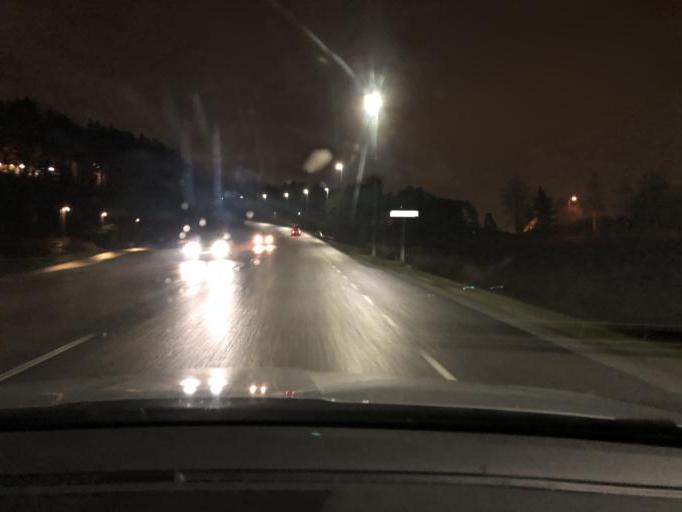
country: SE
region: Stockholm
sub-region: Jarfalla Kommun
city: Jakobsberg
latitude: 59.4047
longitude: 17.8276
